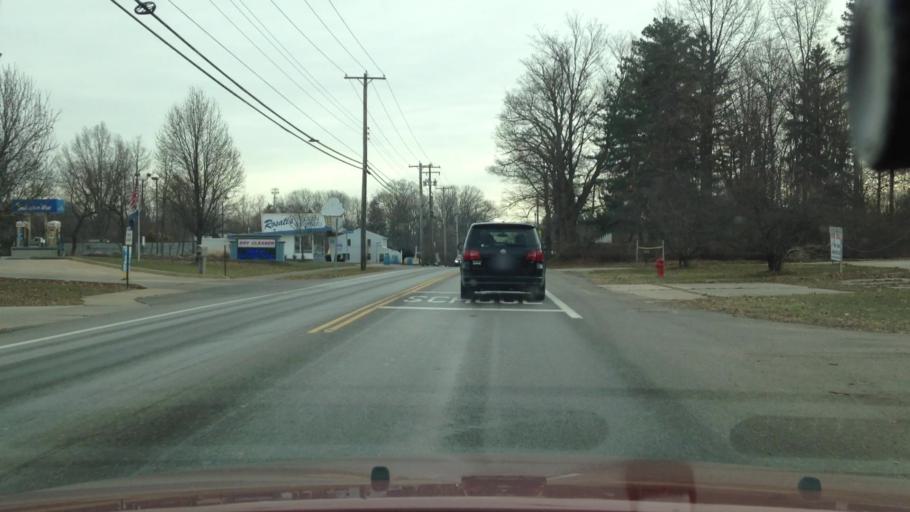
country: US
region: Ohio
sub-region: Summit County
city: Macedonia
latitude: 41.3142
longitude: -81.5365
